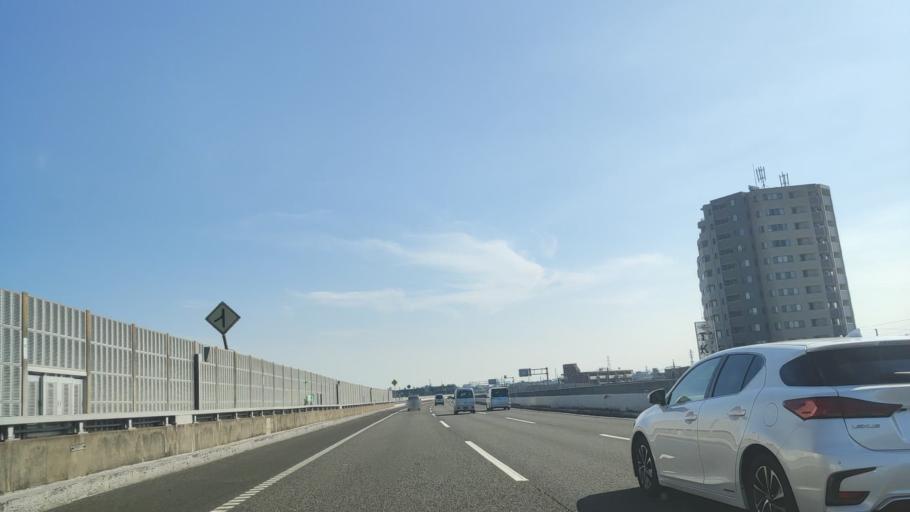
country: JP
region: Tokyo
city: Chofugaoka
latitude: 35.5925
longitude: 139.6269
